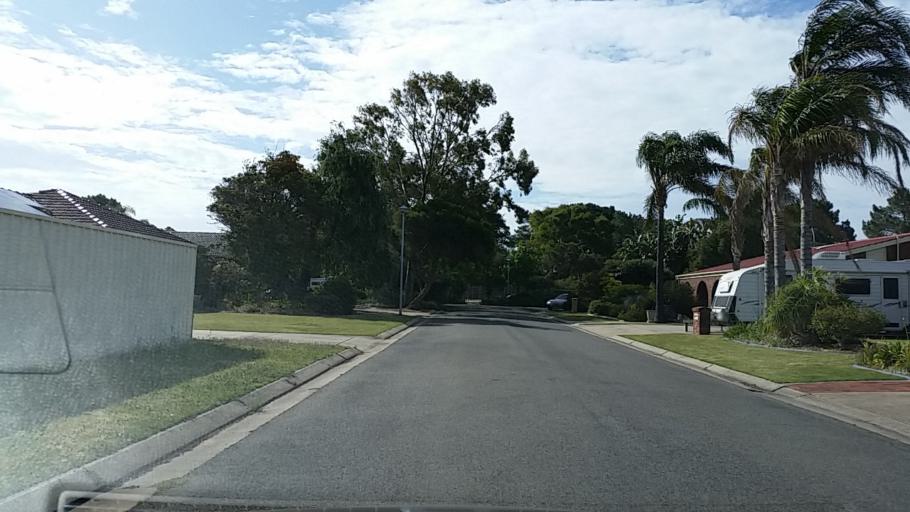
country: AU
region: South Australia
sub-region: Charles Sturt
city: Grange
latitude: -34.8937
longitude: 138.4968
